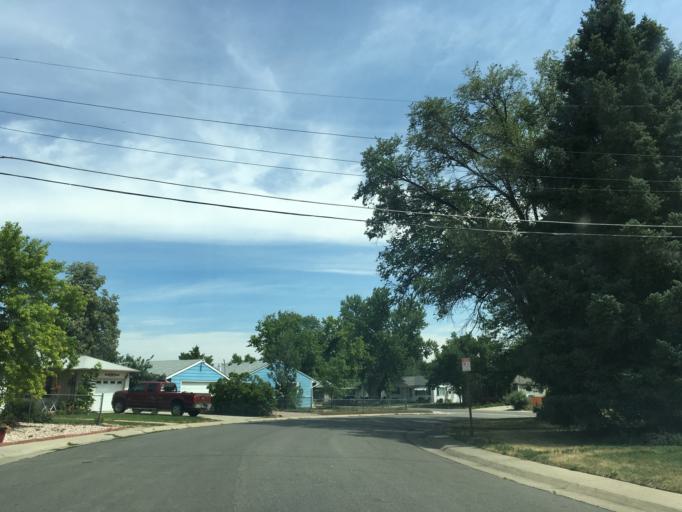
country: US
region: Colorado
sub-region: Jefferson County
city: Lakewood
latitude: 39.6919
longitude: -105.0431
